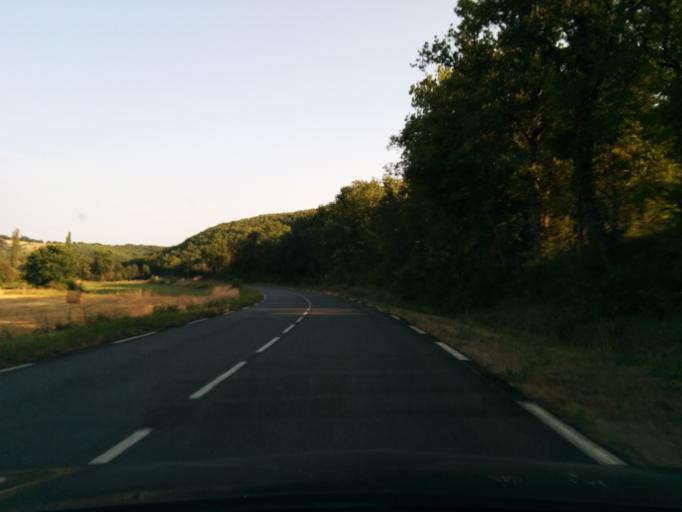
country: FR
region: Midi-Pyrenees
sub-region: Departement du Lot
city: Le Vigan
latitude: 44.6998
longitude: 1.4792
